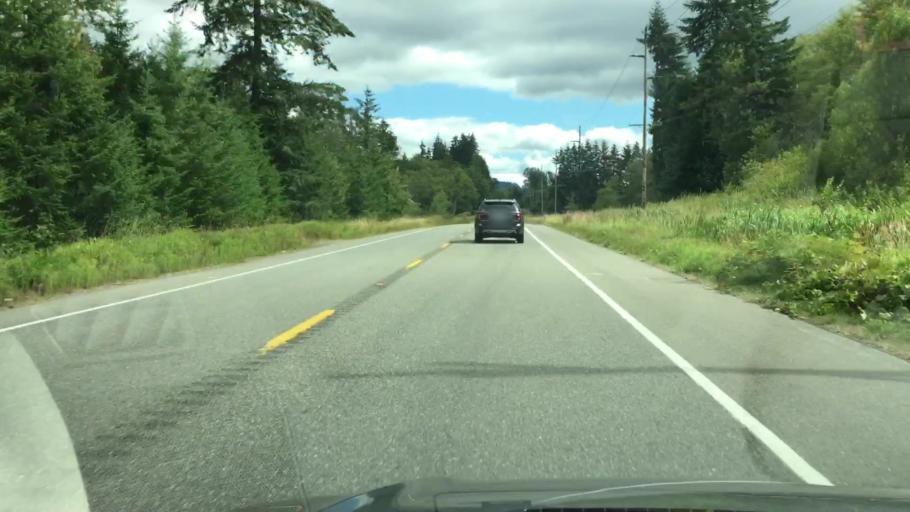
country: US
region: Washington
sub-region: Pierce County
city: Eatonville
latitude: 46.7891
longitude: -122.2608
